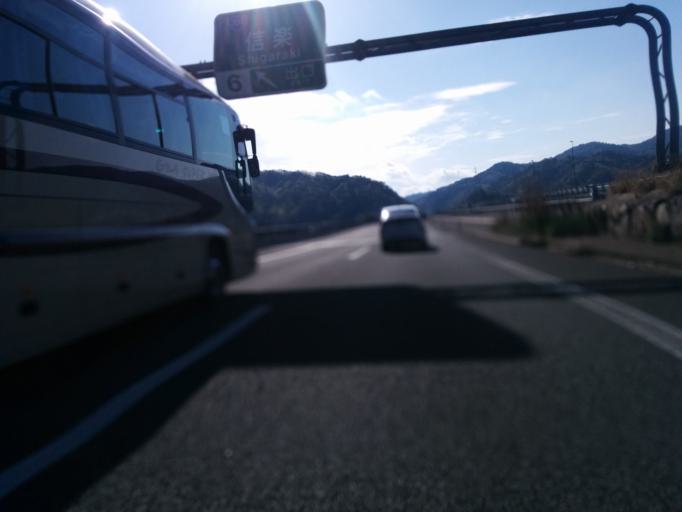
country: JP
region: Shiga Prefecture
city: Minakuchicho-matoba
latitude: 34.9267
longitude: 136.0794
